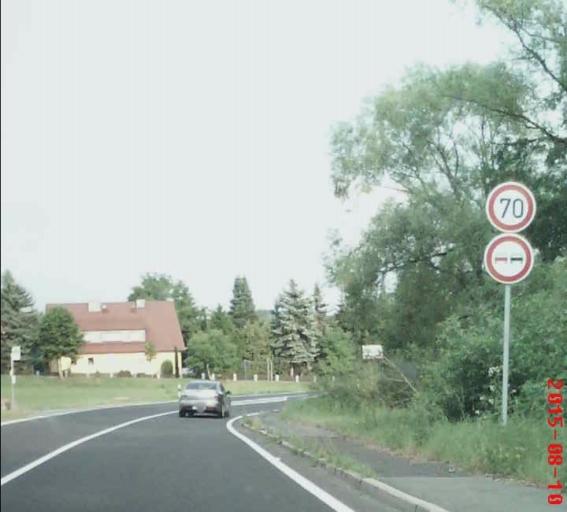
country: DE
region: Thuringia
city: Rohr
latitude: 50.5735
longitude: 10.5090
